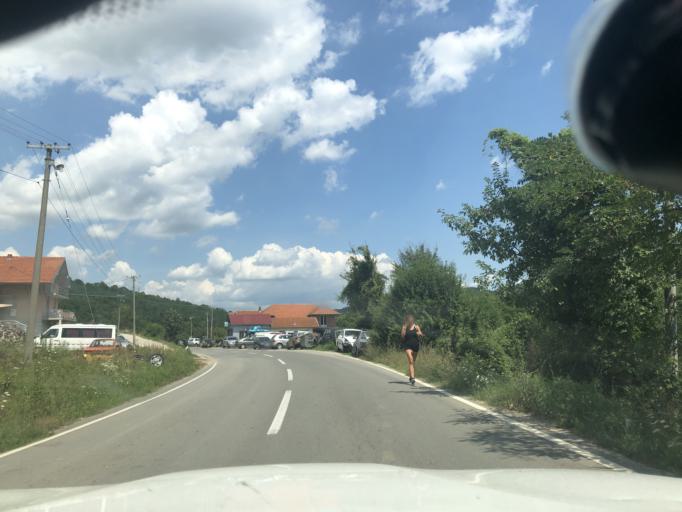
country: RS
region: Central Serbia
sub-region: Jablanicki Okrug
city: Medvega
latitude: 42.8567
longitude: 21.5913
